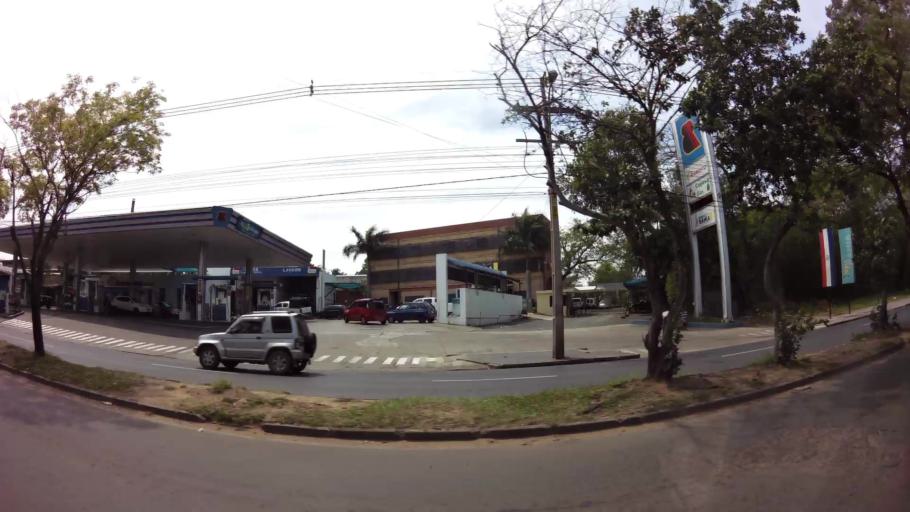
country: PY
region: Asuncion
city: Asuncion
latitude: -25.2676
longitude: -57.5831
